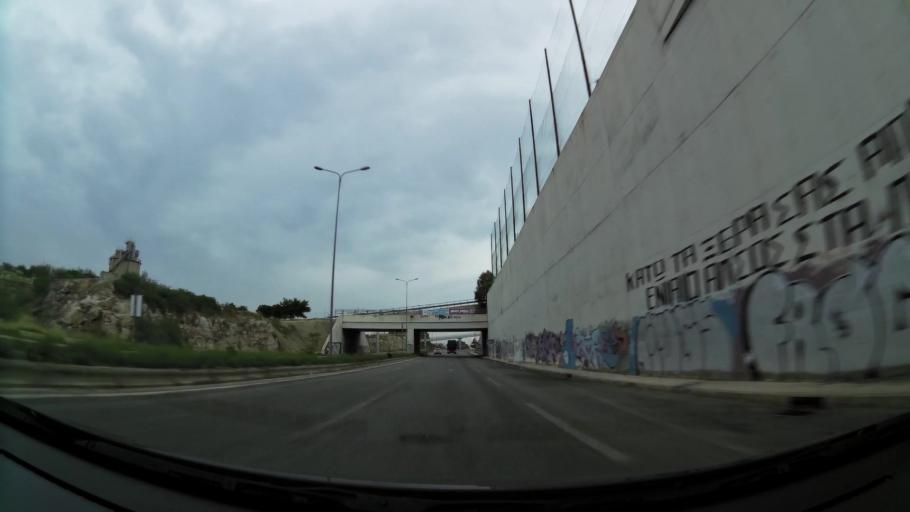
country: GR
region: Attica
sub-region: Nomos Piraios
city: Drapetsona
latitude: 37.9493
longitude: 23.6149
